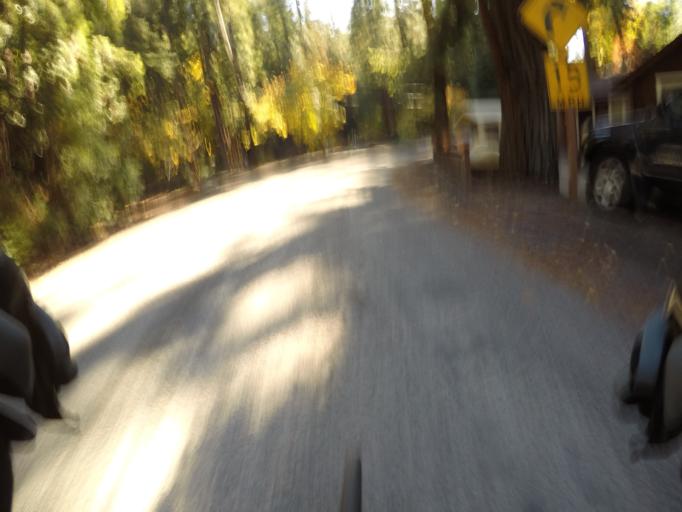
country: US
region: California
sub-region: Santa Cruz County
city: Lompico
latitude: 37.0864
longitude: -122.0469
